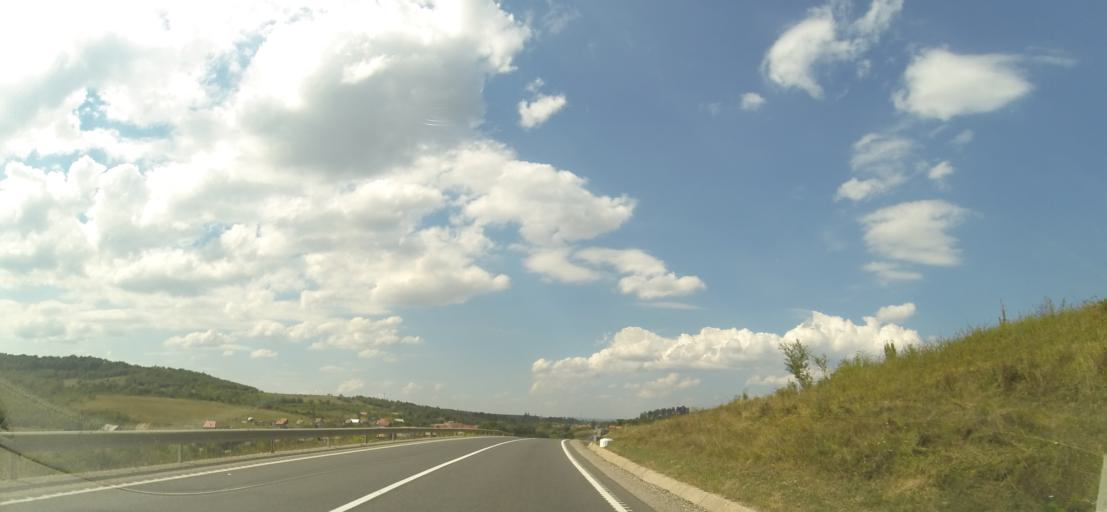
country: RO
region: Brasov
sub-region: Comuna Sinca Veche
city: Persani
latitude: 45.7735
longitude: 25.2240
